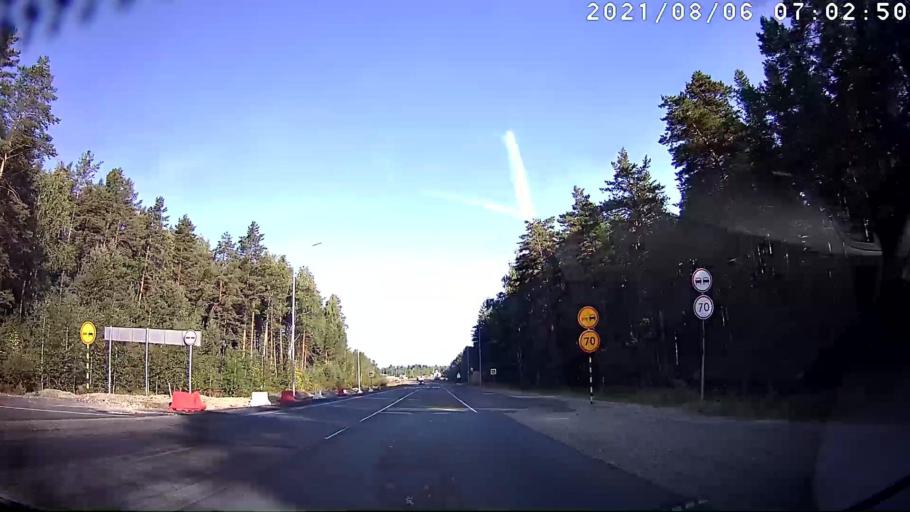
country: RU
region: Mariy-El
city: Yoshkar-Ola
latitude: 56.5375
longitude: 47.9897
